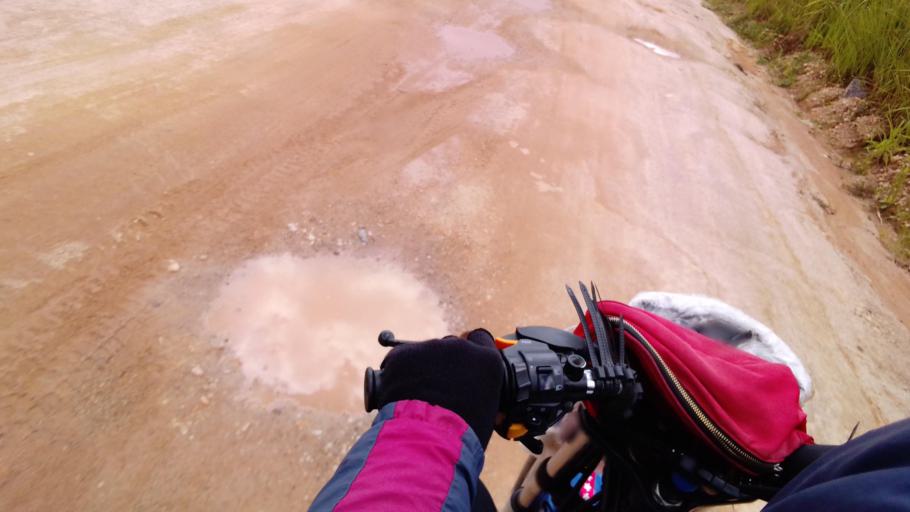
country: SL
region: Eastern Province
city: Koidu
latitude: 8.6741
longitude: -10.9844
